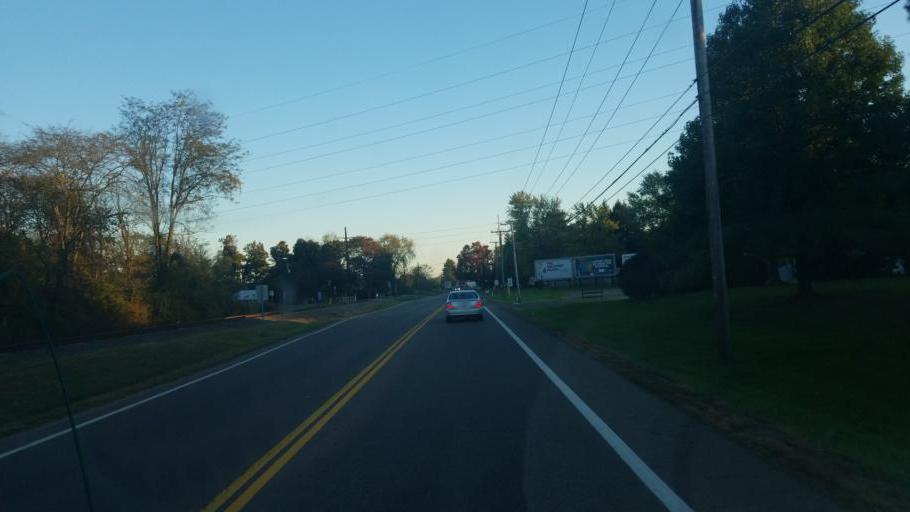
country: US
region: Ohio
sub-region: Licking County
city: Newark
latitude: 40.0933
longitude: -82.4214
